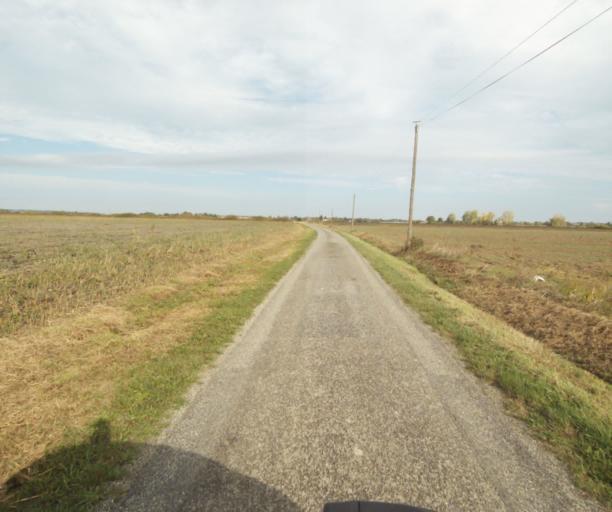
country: FR
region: Midi-Pyrenees
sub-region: Departement du Tarn-et-Garonne
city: Finhan
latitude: 43.9337
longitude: 1.2246
